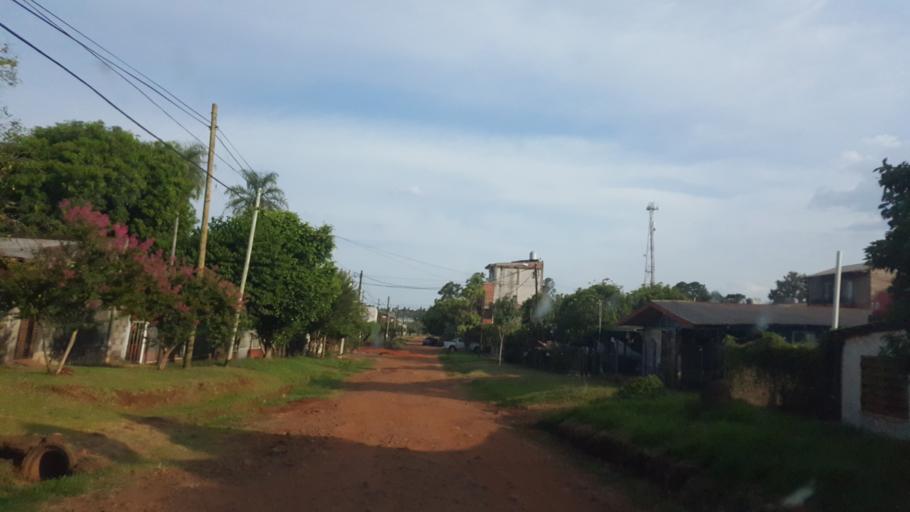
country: AR
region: Misiones
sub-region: Departamento de Capital
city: Posadas
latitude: -27.4331
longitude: -55.8839
